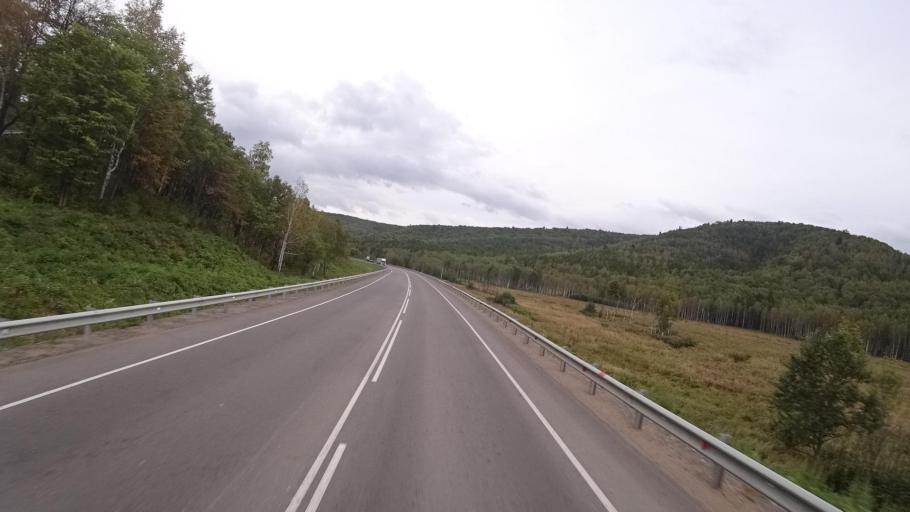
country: RU
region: Jewish Autonomous Oblast
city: Khingansk
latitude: 48.9835
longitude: 131.1609
